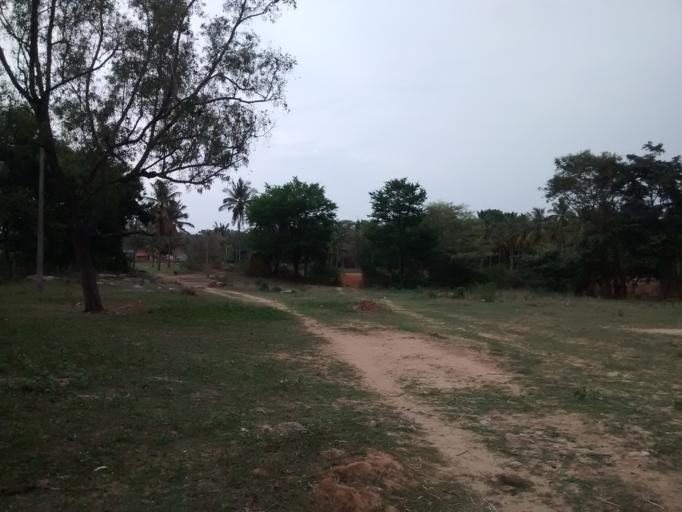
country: IN
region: Karnataka
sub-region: Hassan
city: Hassan
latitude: 12.9449
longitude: 76.1640
